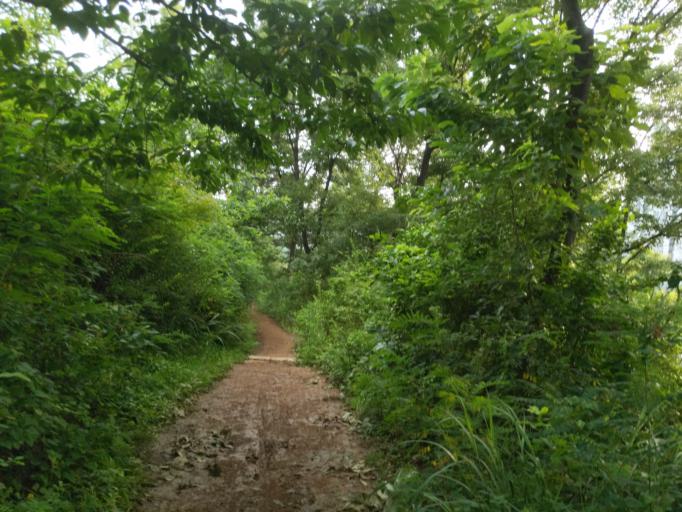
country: KR
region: Daegu
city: Hwawon
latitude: 35.8009
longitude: 128.5271
